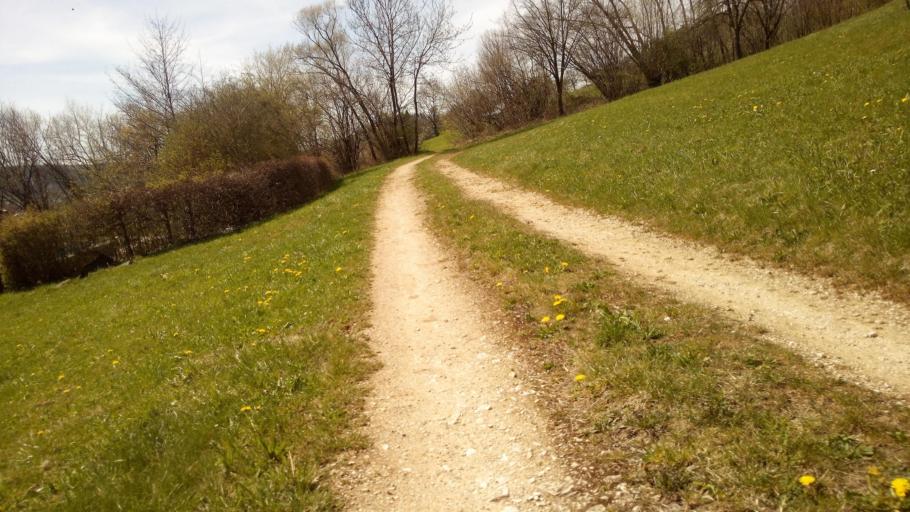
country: DE
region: Baden-Wuerttemberg
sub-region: Regierungsbezirk Stuttgart
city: Donzdorf
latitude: 48.6989
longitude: 9.8175
